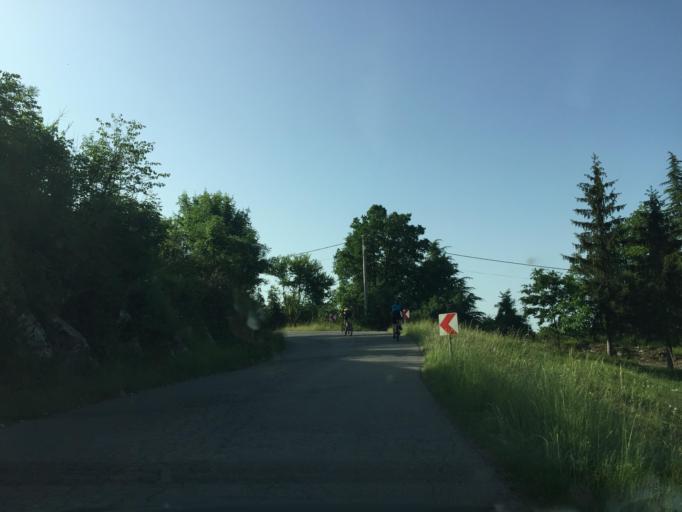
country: HR
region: Primorsko-Goranska
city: Kastav
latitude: 45.4186
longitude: 14.3130
